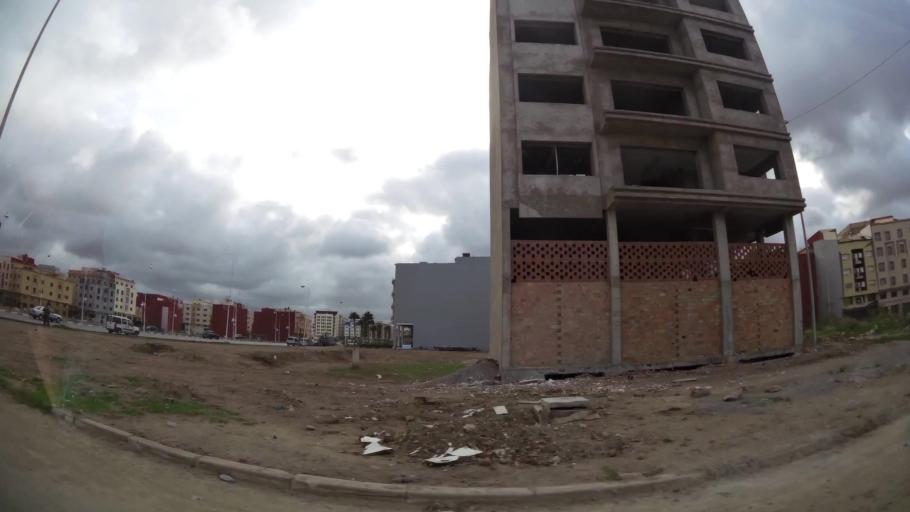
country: MA
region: Oriental
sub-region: Nador
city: Nador
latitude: 35.1530
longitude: -2.9247
